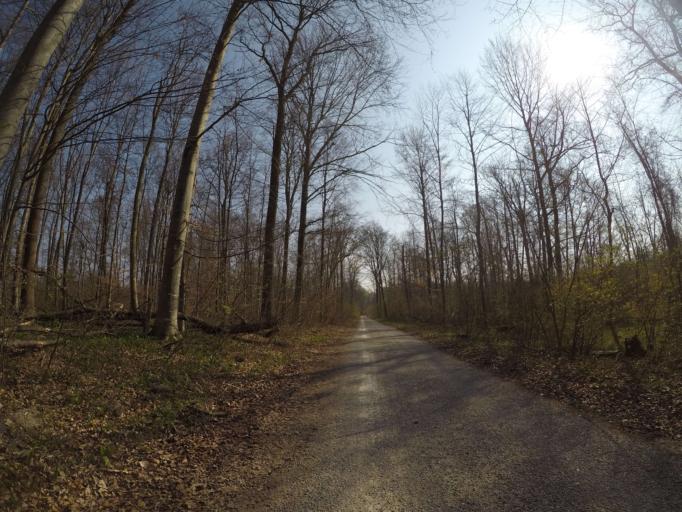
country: DE
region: Bavaria
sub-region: Swabia
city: Leipheim
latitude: 48.4507
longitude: 10.1967
